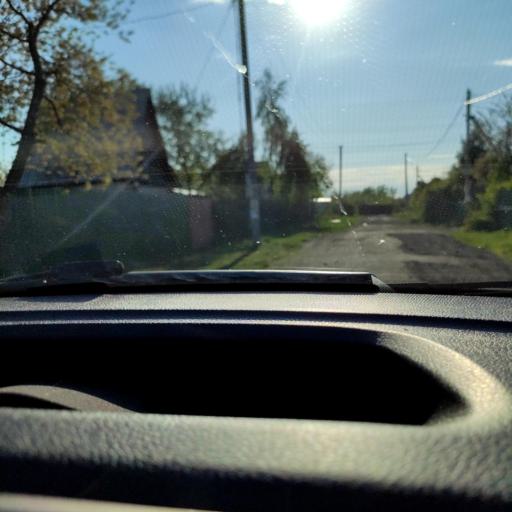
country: RU
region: Samara
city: Tol'yatti
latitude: 53.5838
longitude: 49.2973
